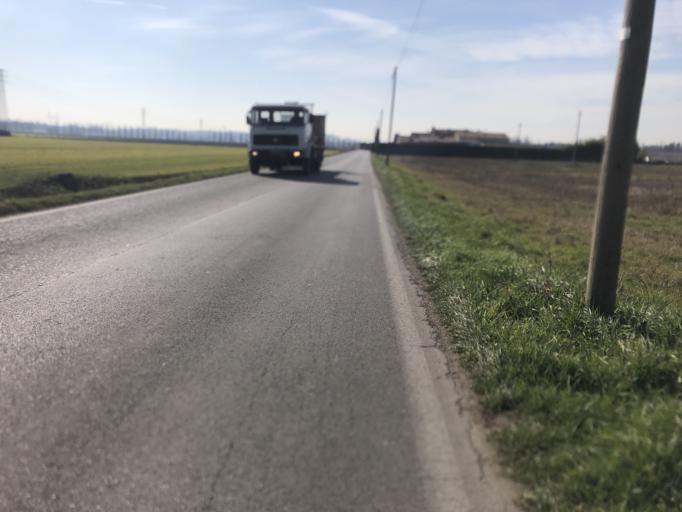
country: IT
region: Veneto
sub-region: Provincia di Verona
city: San Giorgio in Salici
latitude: 45.4120
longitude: 10.8003
